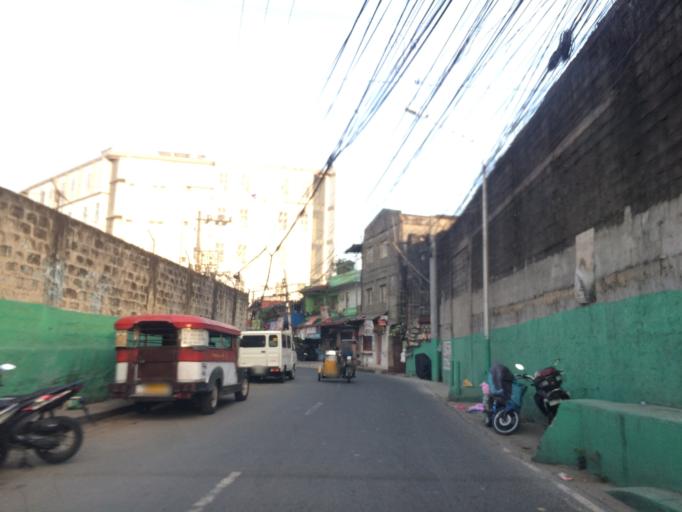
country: PH
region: Calabarzon
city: Bagong Pagasa
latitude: 14.6688
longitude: 121.0128
